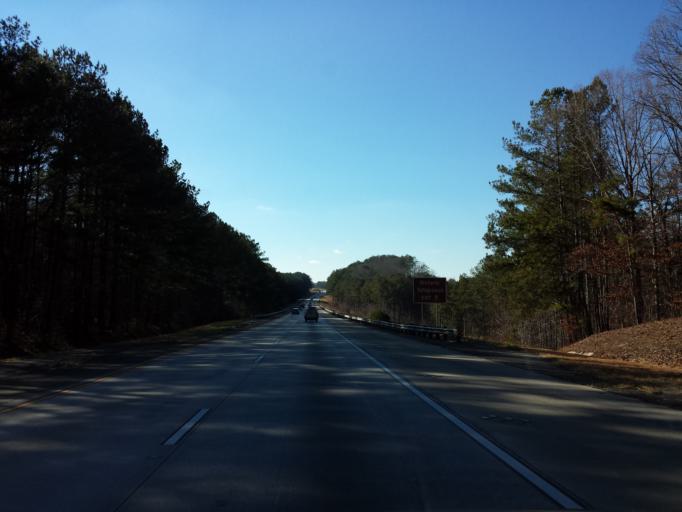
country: US
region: Georgia
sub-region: Haralson County
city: Tallapoosa
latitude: 33.6874
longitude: -85.2496
